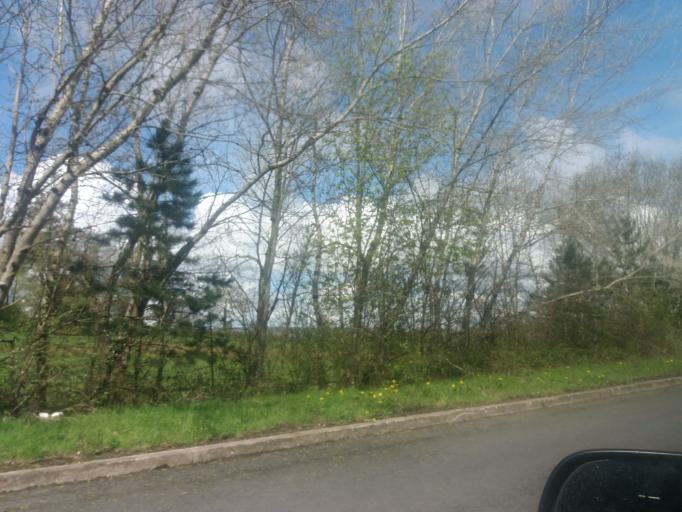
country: IE
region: Ulster
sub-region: An Cabhan
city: Belturbet
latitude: 54.1207
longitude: -7.4815
